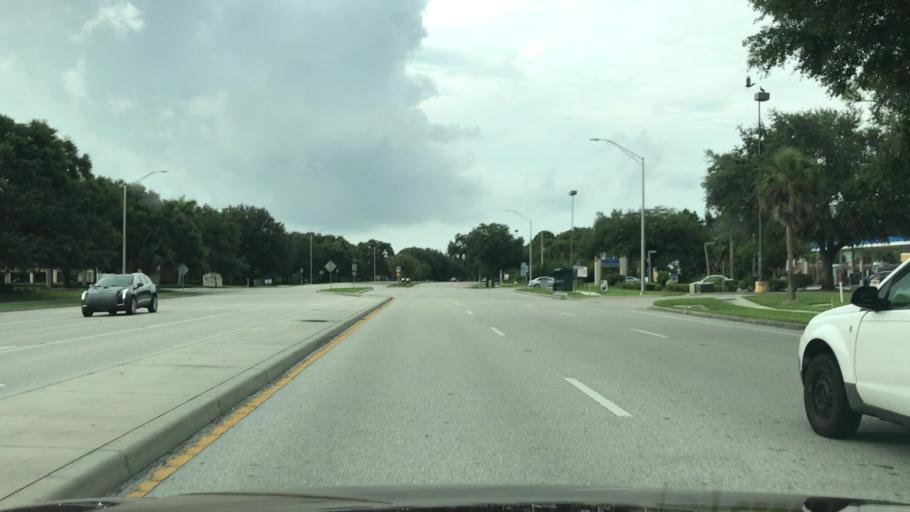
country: US
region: Florida
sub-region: Sarasota County
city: Plantation
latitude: 27.0799
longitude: -82.3888
